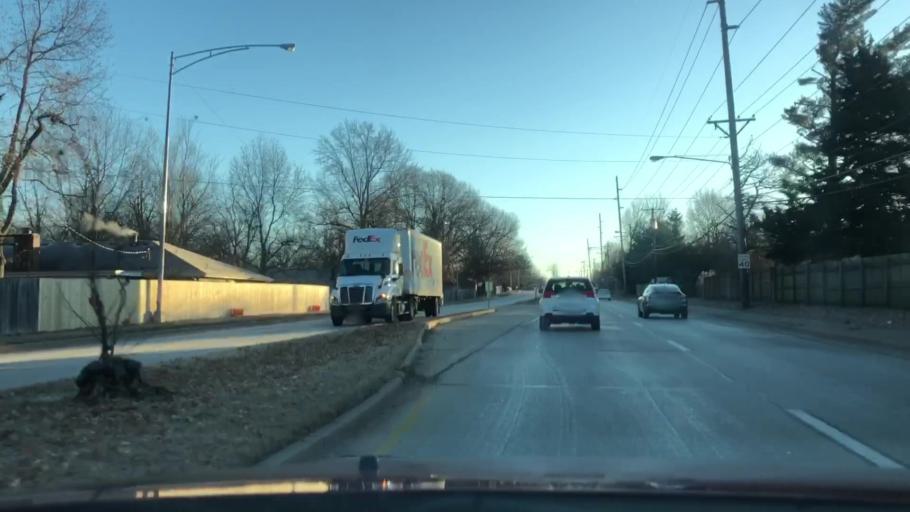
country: US
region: Missouri
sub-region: Greene County
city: Springfield
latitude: 37.1590
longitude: -93.2550
